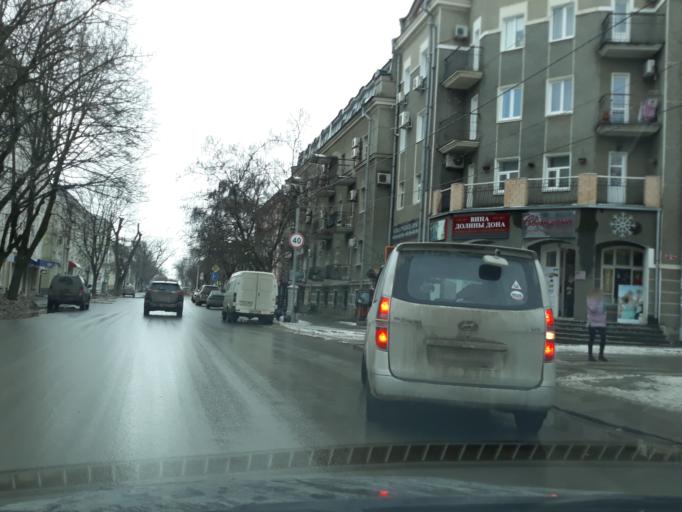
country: RU
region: Rostov
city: Taganrog
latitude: 47.2104
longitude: 38.9370
